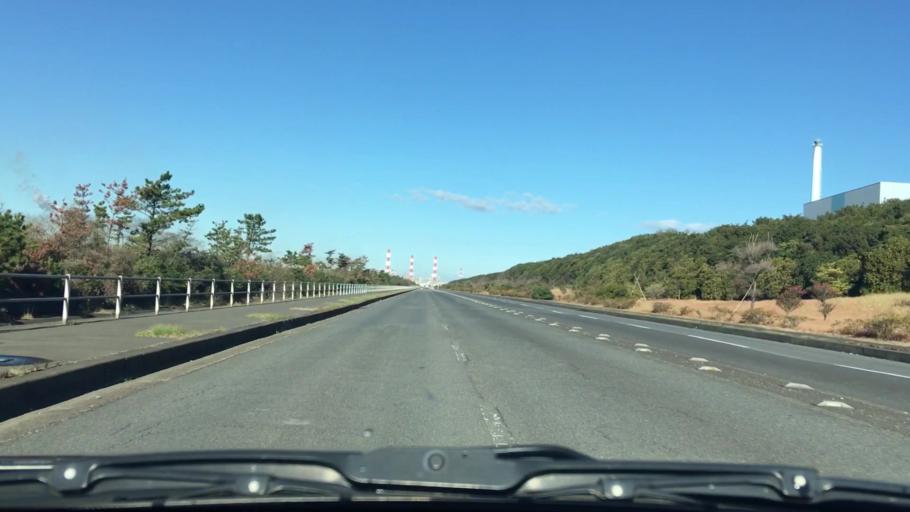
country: JP
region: Chiba
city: Omigawa
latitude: 35.8742
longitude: 140.7343
